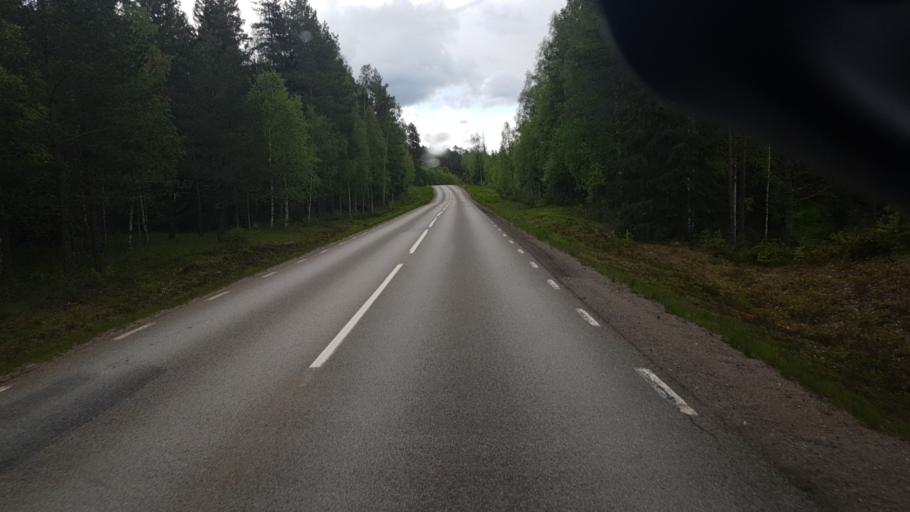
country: SE
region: Vaermland
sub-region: Arjangs Kommun
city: Arjaeng
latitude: 59.5562
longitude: 12.1607
